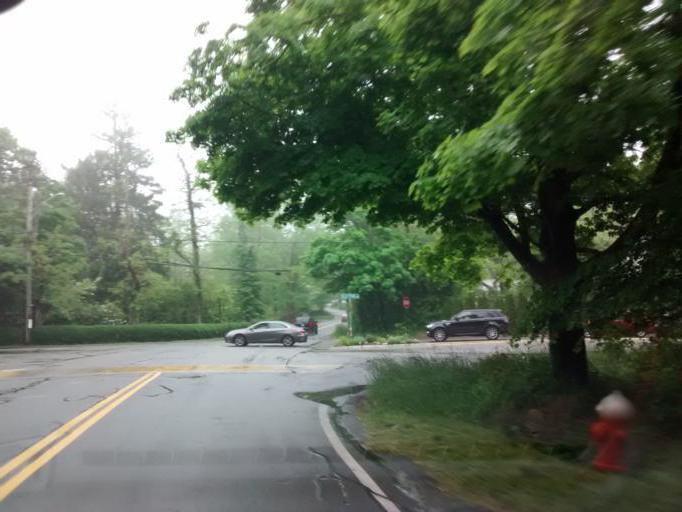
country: US
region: Massachusetts
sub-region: Barnstable County
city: Monument Beach
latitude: 41.7177
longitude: -70.6090
